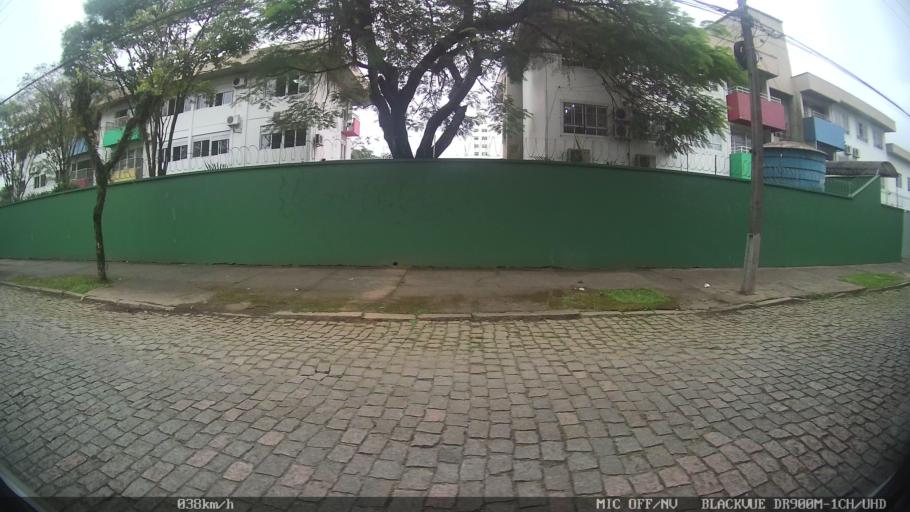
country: BR
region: Santa Catarina
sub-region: Joinville
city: Joinville
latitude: -26.3118
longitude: -48.8396
